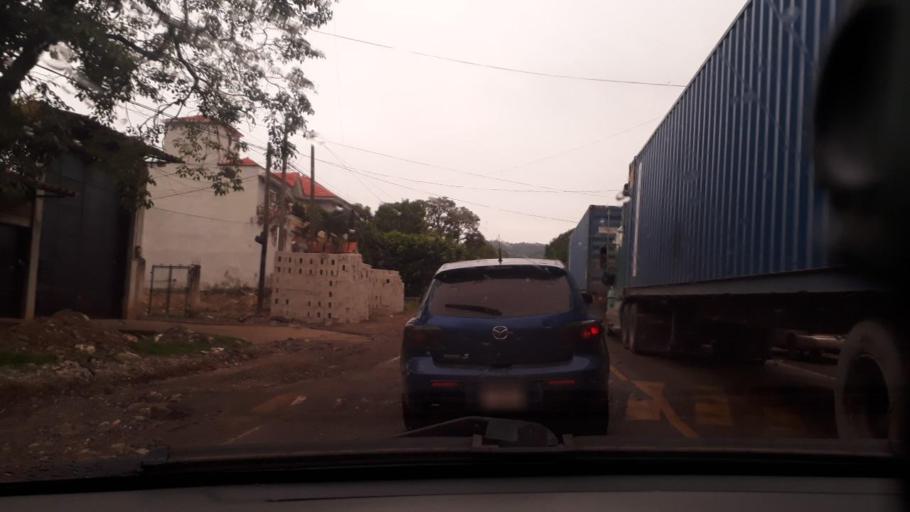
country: GT
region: Jutiapa
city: Atescatempa
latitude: 14.1917
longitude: -89.6715
